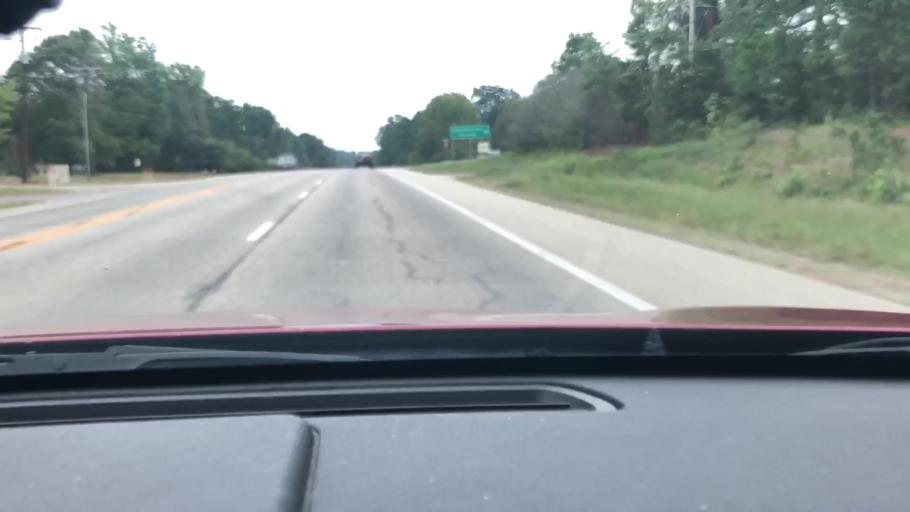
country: US
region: Arkansas
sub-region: Miller County
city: Texarkana
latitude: 33.4296
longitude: -93.9609
